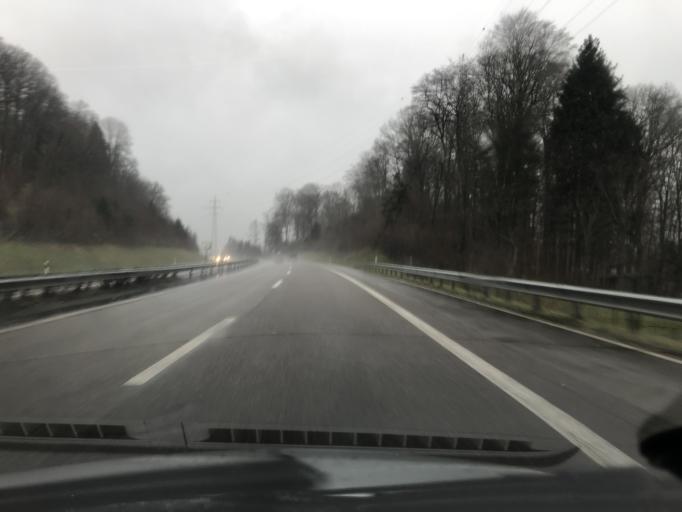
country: CH
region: Aargau
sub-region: Bezirk Aarau
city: Suhr
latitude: 47.3635
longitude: 8.0734
